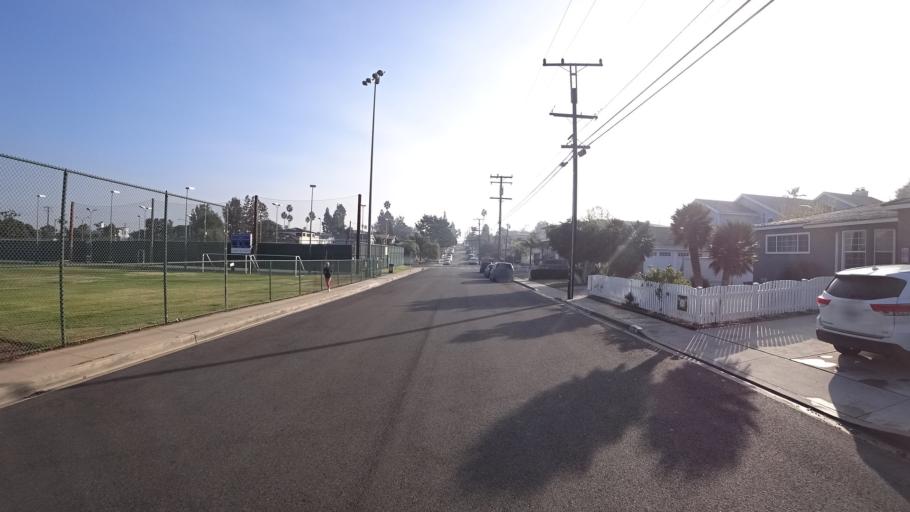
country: US
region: California
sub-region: Los Angeles County
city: Manhattan Beach
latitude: 33.8865
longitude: -118.3840
